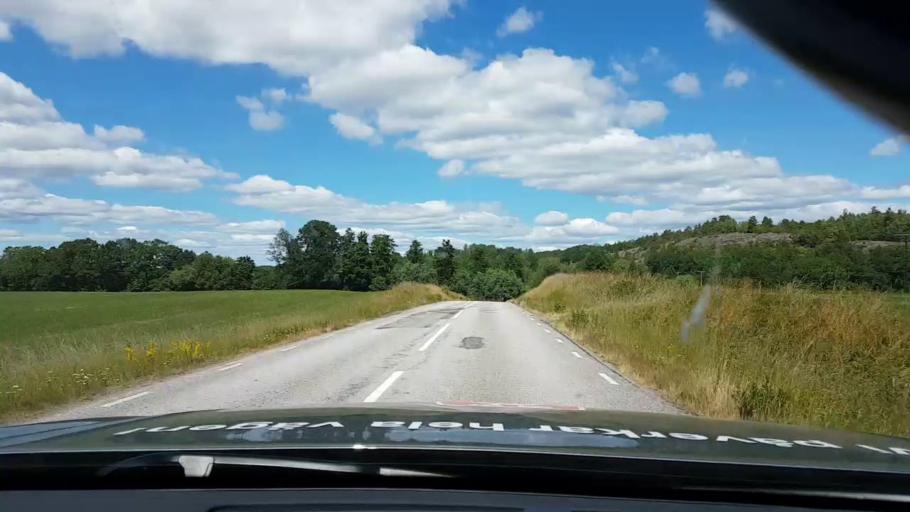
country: SE
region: Kalmar
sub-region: Vasterviks Kommun
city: Overum
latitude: 58.0526
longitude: 16.4058
